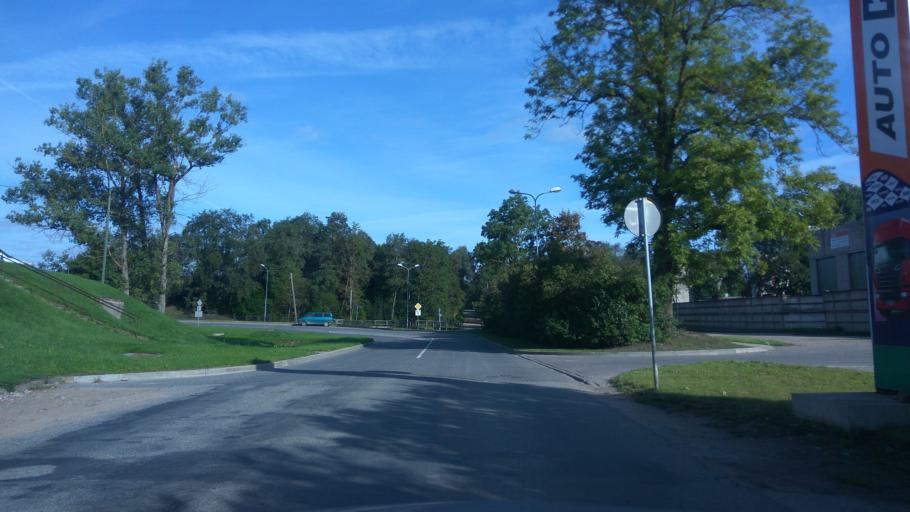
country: LV
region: Kuldigas Rajons
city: Kuldiga
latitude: 56.9777
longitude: 21.9615
